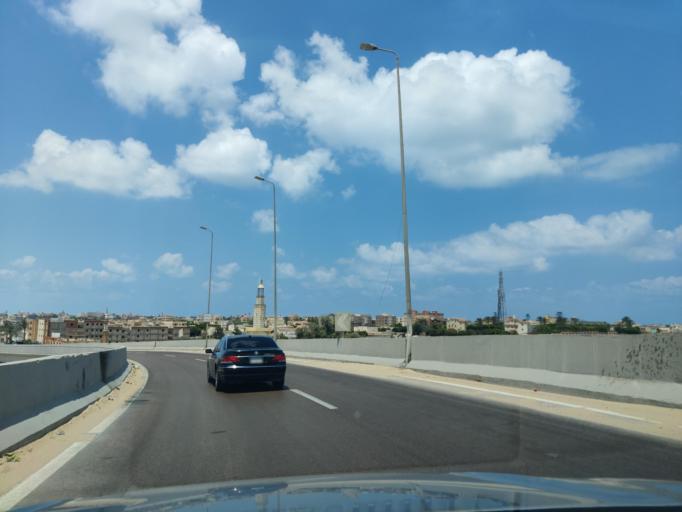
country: EG
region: Alexandria
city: Alexandria
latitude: 31.0127
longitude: 29.6326
